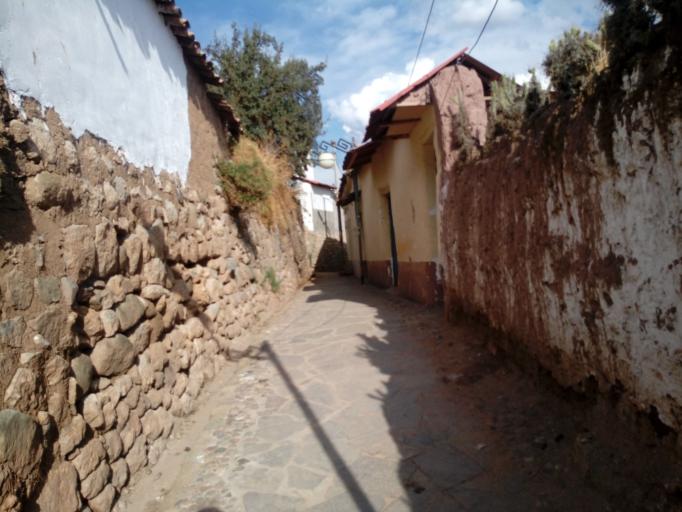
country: PE
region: Cusco
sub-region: Provincia de Cusco
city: Cusco
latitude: -13.5141
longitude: -71.9733
